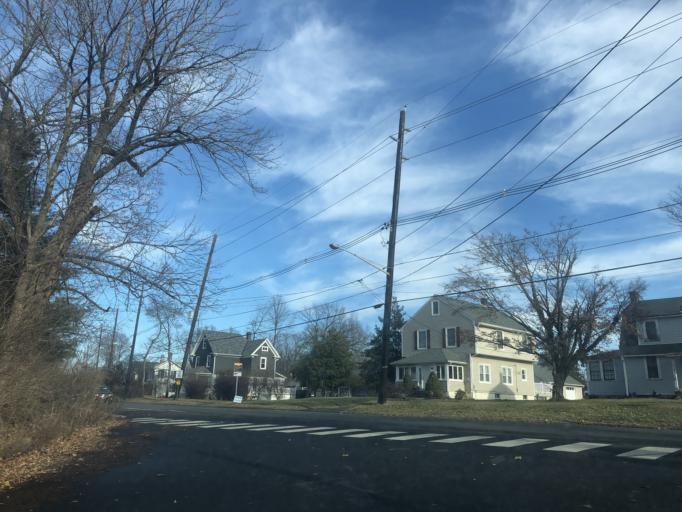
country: US
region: New Jersey
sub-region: Somerset County
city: Kingston
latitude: 40.3779
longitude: -74.6155
